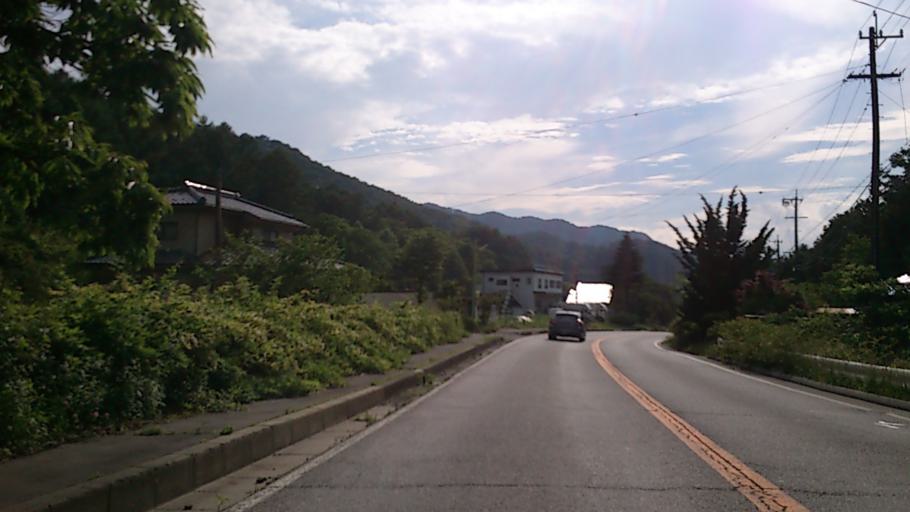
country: JP
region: Nagano
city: Saku
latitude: 36.2182
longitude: 138.5735
